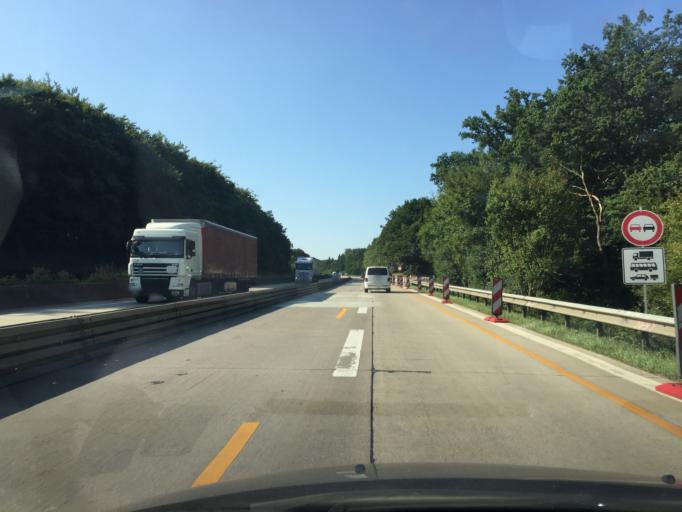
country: DE
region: Lower Saxony
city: Garlstorf
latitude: 53.2296
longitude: 10.0762
